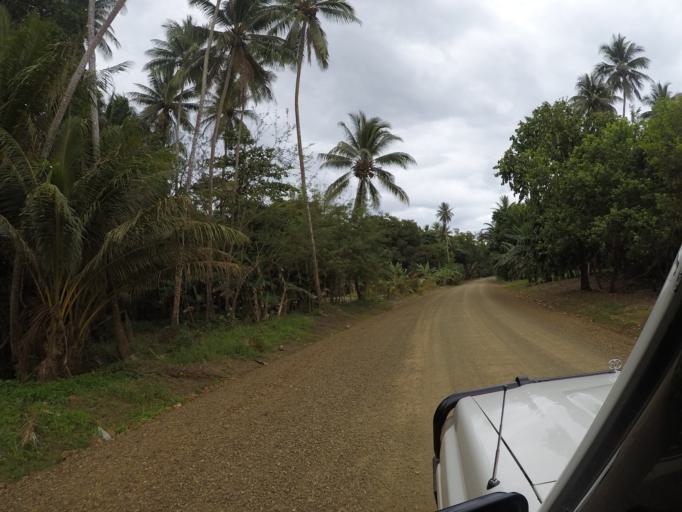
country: PG
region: Milne Bay
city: Alotau
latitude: -10.2849
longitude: 150.7716
